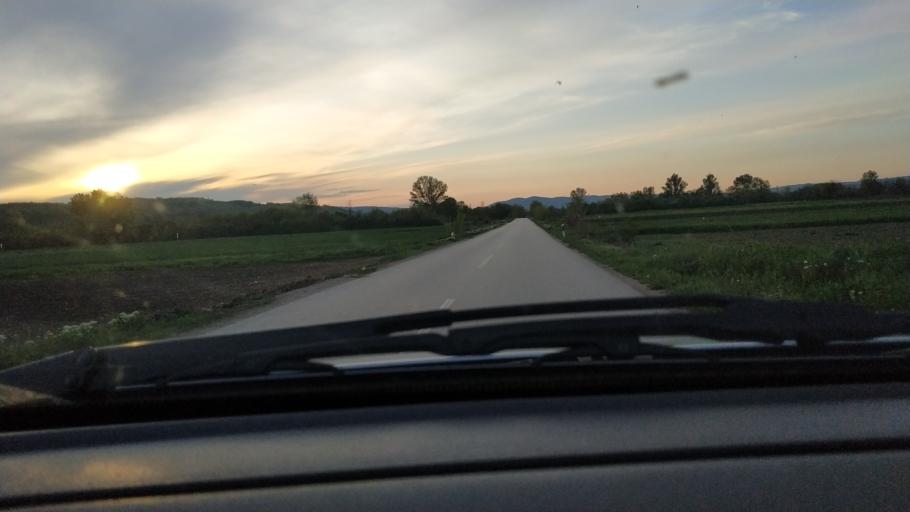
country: RS
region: Central Serbia
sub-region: Nisavski Okrug
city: Aleksinac
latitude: 43.5475
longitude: 21.6221
